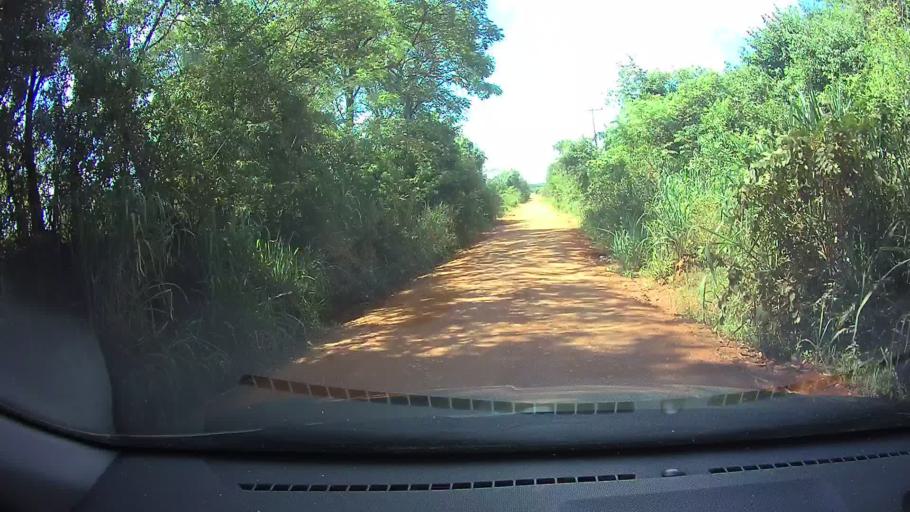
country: PY
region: Paraguari
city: La Colmena
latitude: -25.9029
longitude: -56.7933
